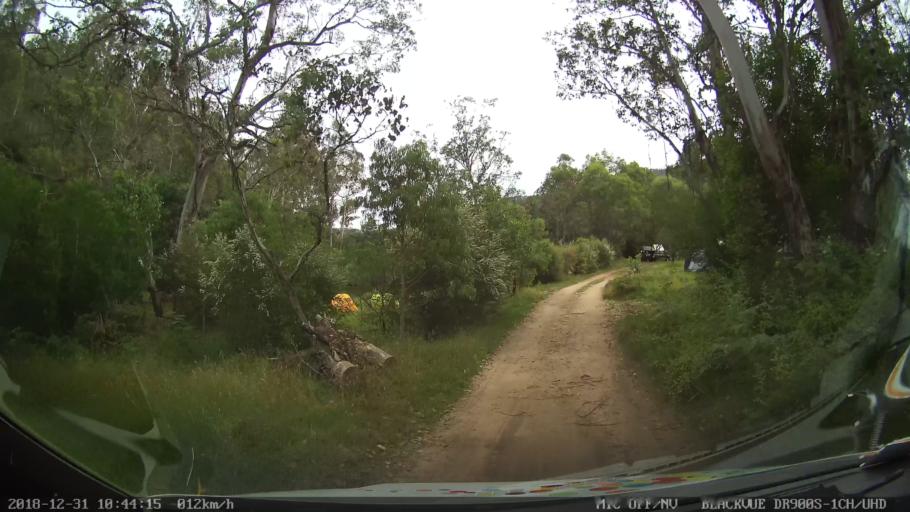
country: AU
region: New South Wales
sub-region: Snowy River
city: Jindabyne
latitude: -36.3792
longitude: 148.1780
